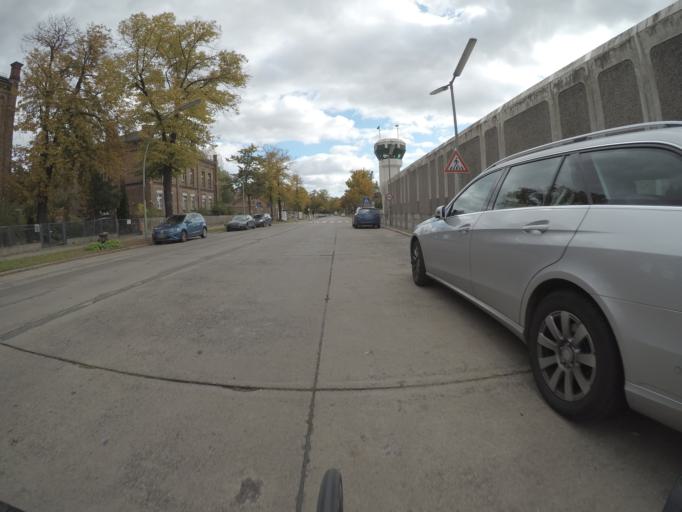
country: DE
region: Berlin
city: Moabit
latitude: 52.5393
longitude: 13.3205
